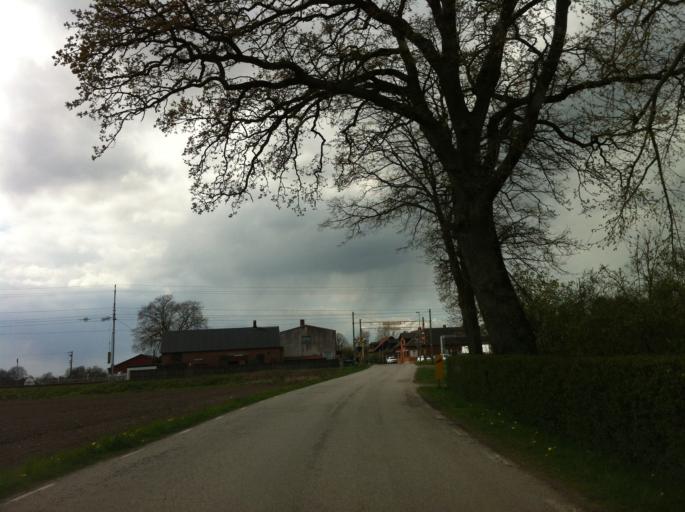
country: SE
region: Skane
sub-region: Kavlinge Kommun
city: Kaevlinge
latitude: 55.8202
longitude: 13.1170
